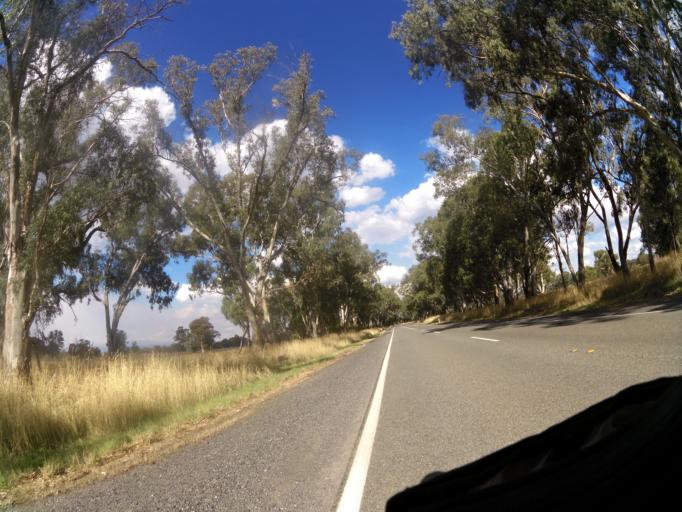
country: AU
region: Victoria
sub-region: Mansfield
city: Mansfield
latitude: -37.0025
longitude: 146.0754
